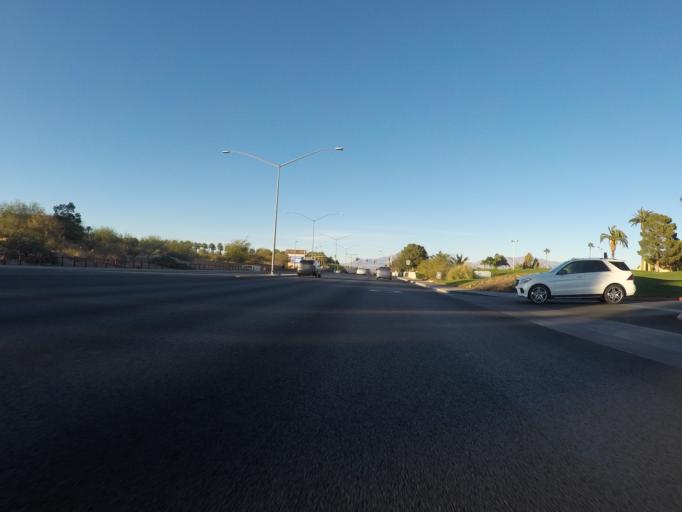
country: US
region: Nevada
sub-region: Clark County
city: Summerlin South
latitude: 36.1724
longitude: -115.2870
